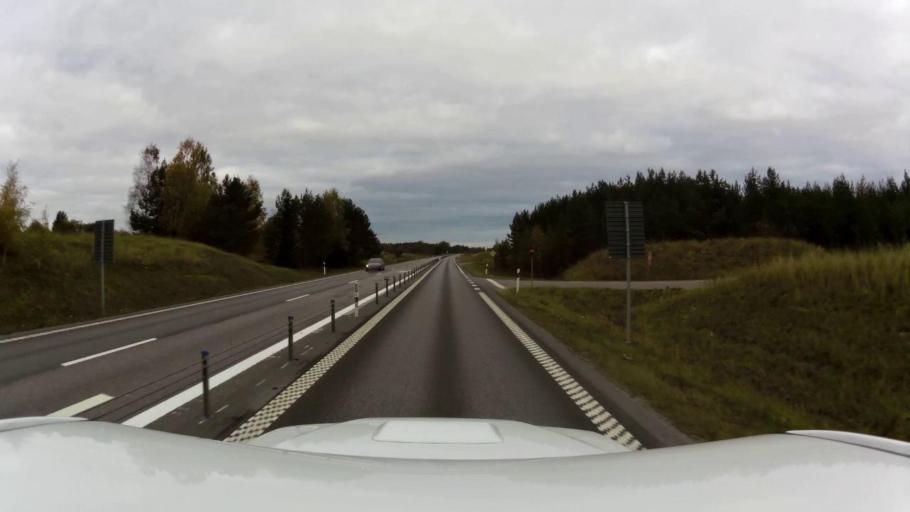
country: SE
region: OEstergoetland
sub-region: Linkopings Kommun
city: Ljungsbro
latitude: 58.4946
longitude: 15.4636
